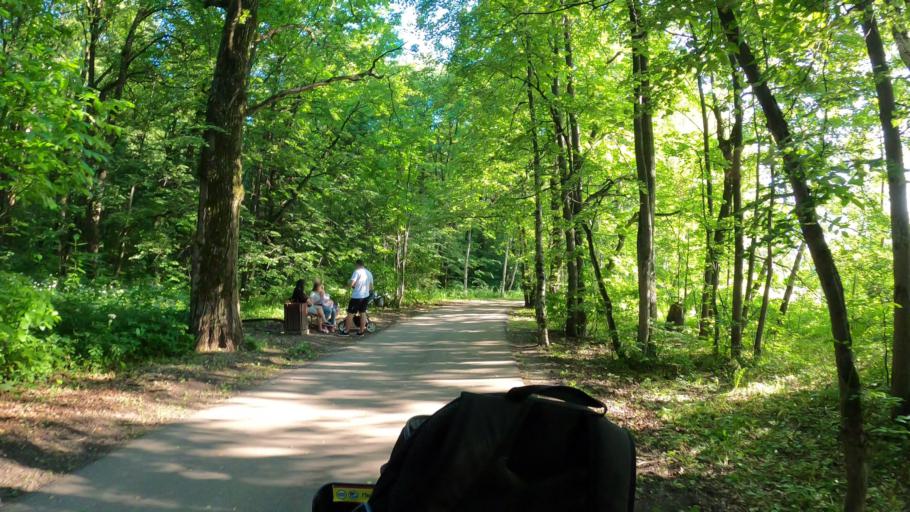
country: RU
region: Moscow
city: Yasenevo
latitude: 55.6148
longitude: 37.5561
